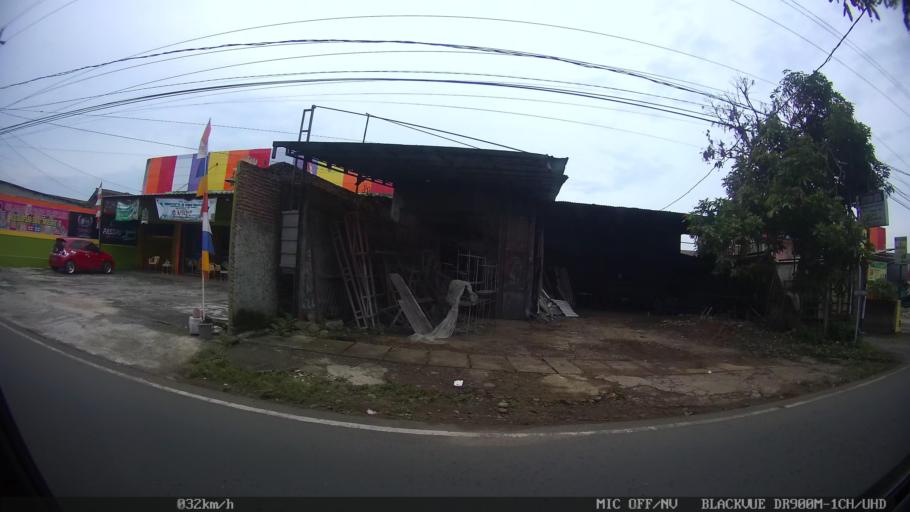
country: ID
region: Lampung
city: Kedaton
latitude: -5.3907
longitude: 105.2386
